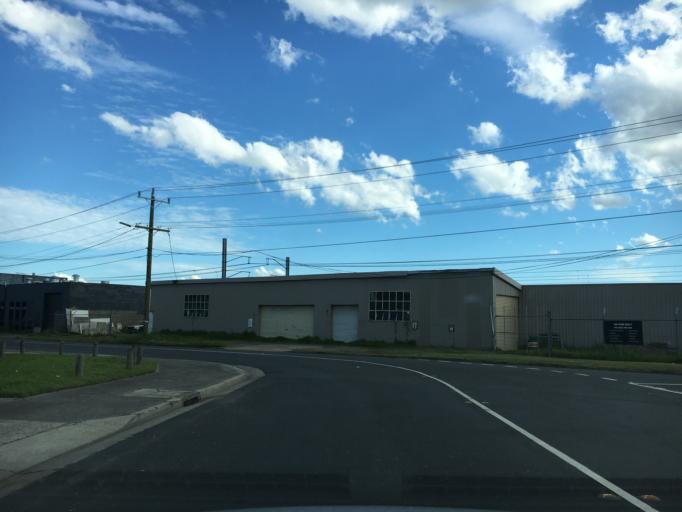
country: AU
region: Victoria
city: Clayton
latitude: -37.9154
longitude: 145.1091
